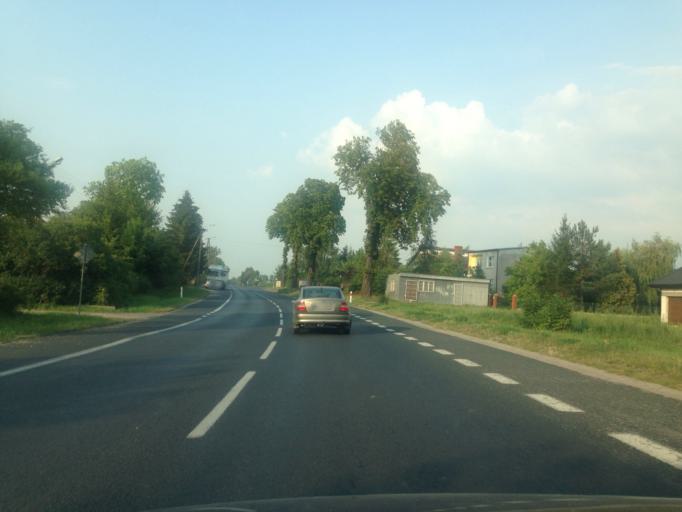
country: PL
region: Kujawsko-Pomorskie
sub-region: Powiat lipnowski
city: Lipno
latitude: 52.8114
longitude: 19.1386
